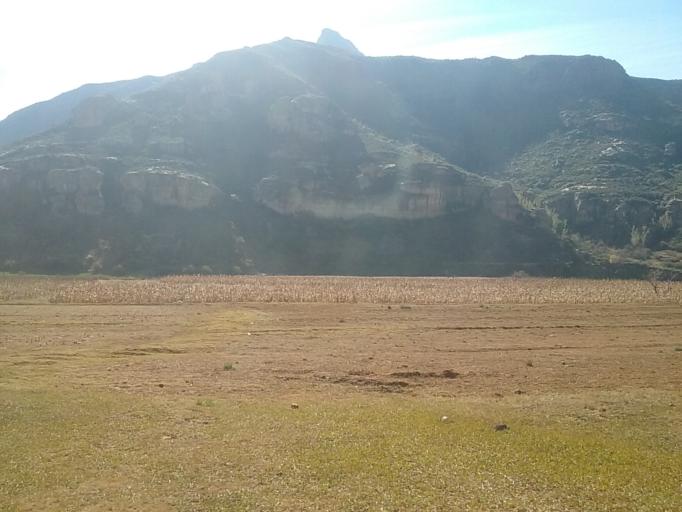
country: LS
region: Berea
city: Teyateyaneng
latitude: -29.2508
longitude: 27.9172
